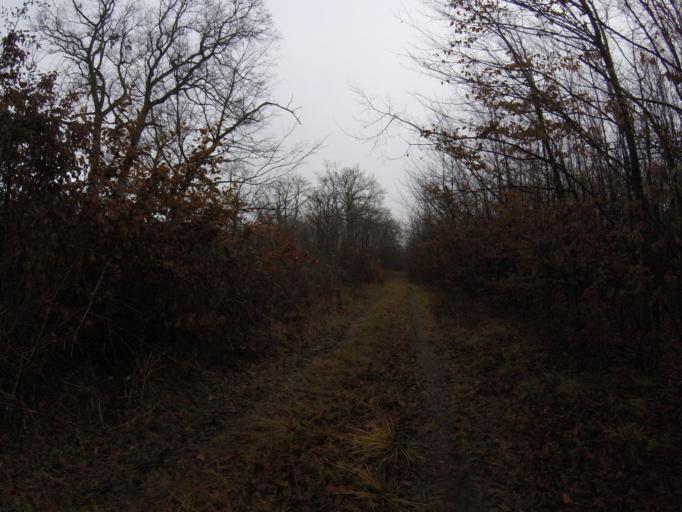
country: HU
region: Vas
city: Sarvar
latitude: 47.2336
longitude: 17.0078
